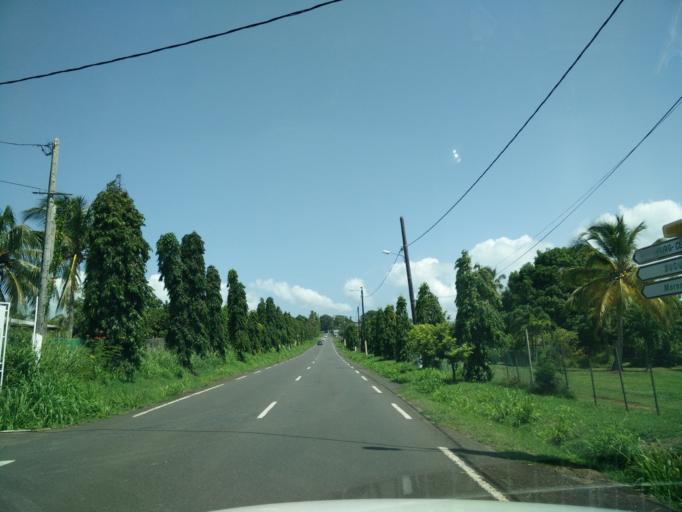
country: GP
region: Guadeloupe
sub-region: Guadeloupe
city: Petit-Bourg
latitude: 16.1795
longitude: -61.5874
